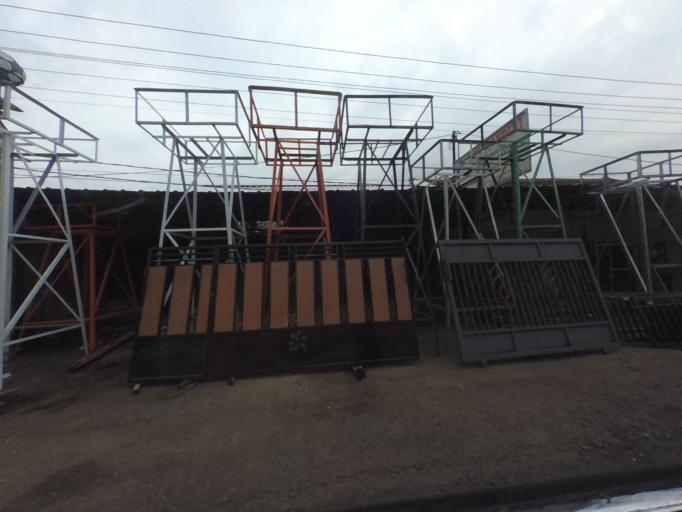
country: ID
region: West Java
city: Cicurug
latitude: -6.8328
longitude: 106.7615
